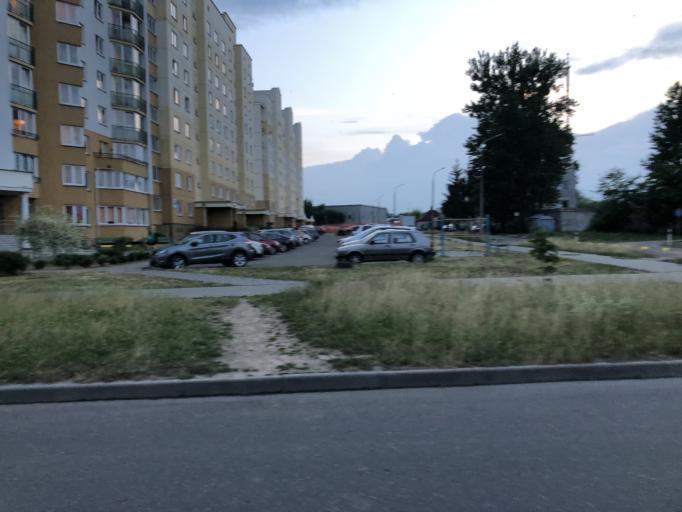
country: BY
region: Grodnenskaya
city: Hrodna
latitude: 53.6990
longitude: 23.8353
